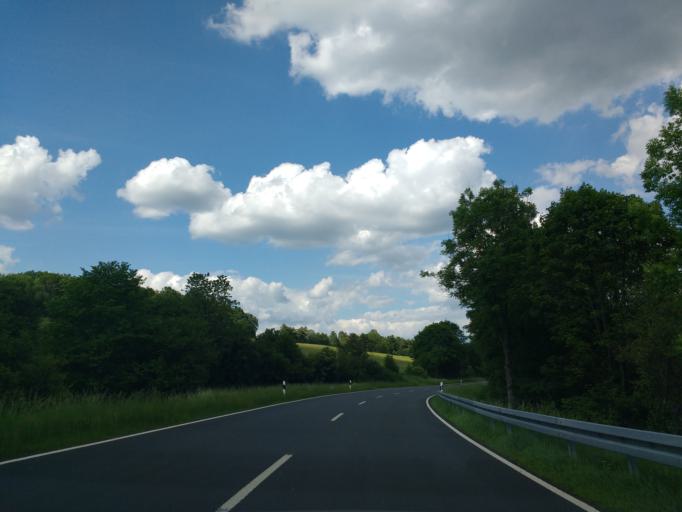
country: DE
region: Hesse
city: Hatzfeld
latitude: 50.9589
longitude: 8.5747
